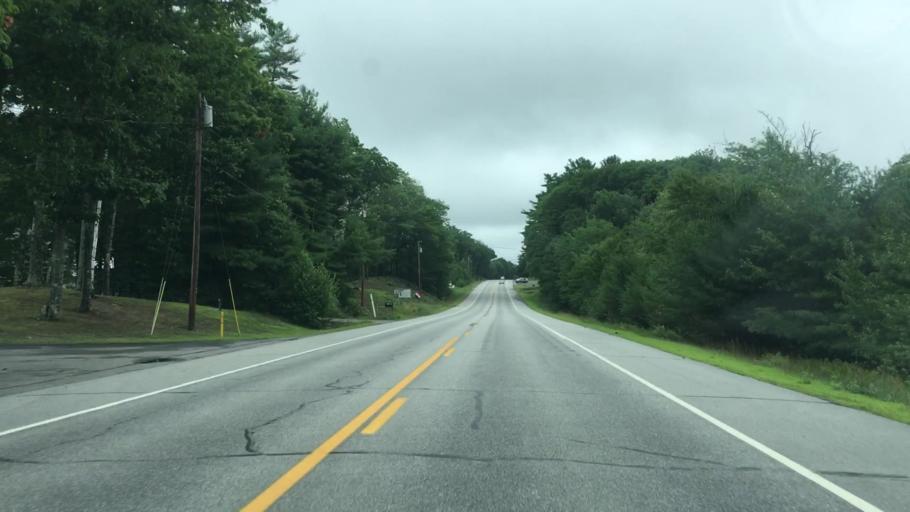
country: US
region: Maine
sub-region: Kennebec County
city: Windsor
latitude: 44.2773
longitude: -69.6296
